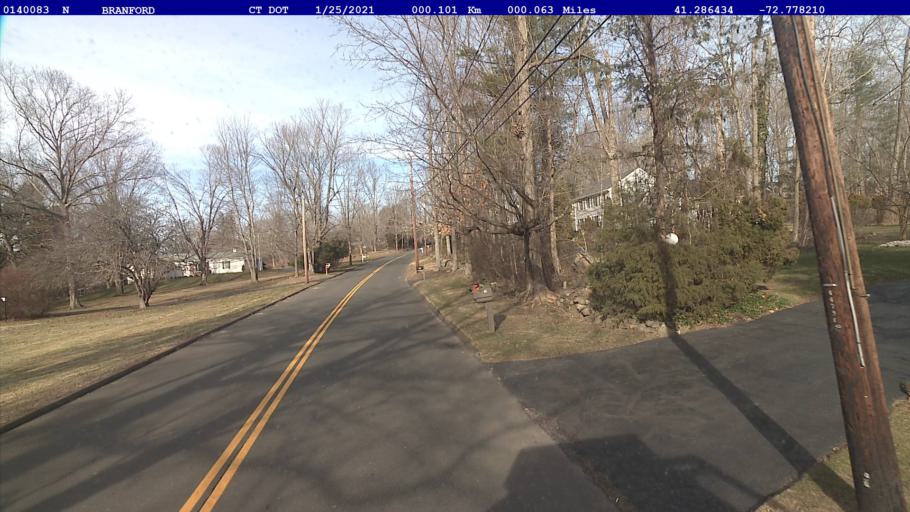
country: US
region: Connecticut
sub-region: New Haven County
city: Branford
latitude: 41.2864
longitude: -72.7782
